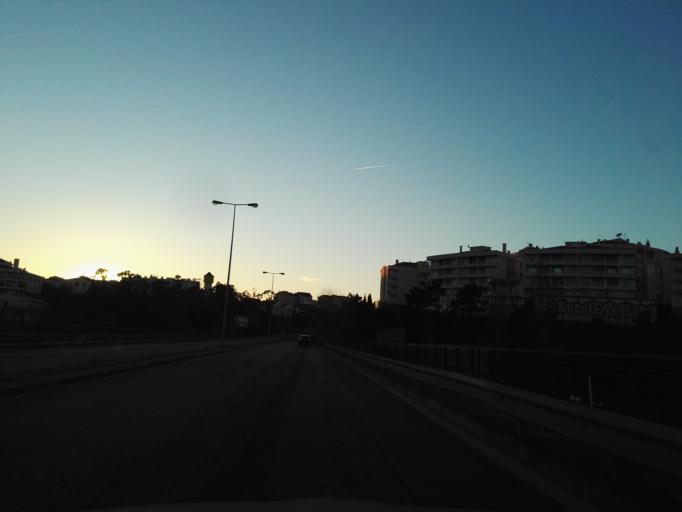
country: PT
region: Setubal
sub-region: Seixal
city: Corroios
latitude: 38.6450
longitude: -9.1524
